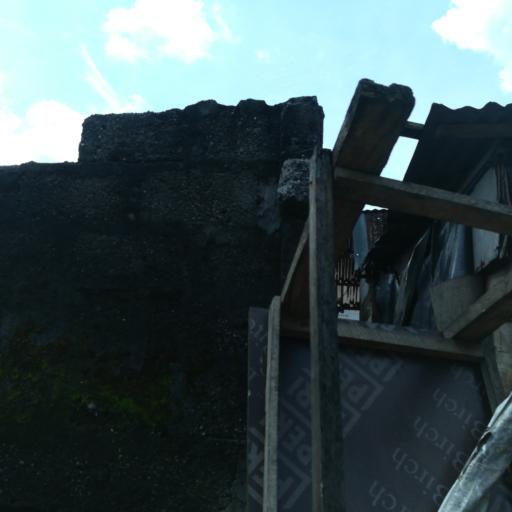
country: NG
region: Rivers
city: Okrika
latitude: 4.7766
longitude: 7.0604
